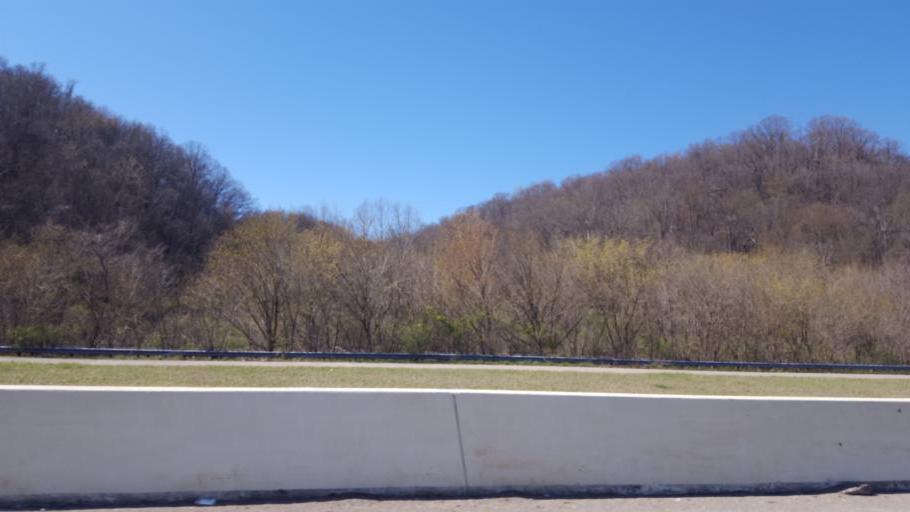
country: US
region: Ohio
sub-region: Jefferson County
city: Tiltonsville
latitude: 40.2053
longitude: -80.6718
